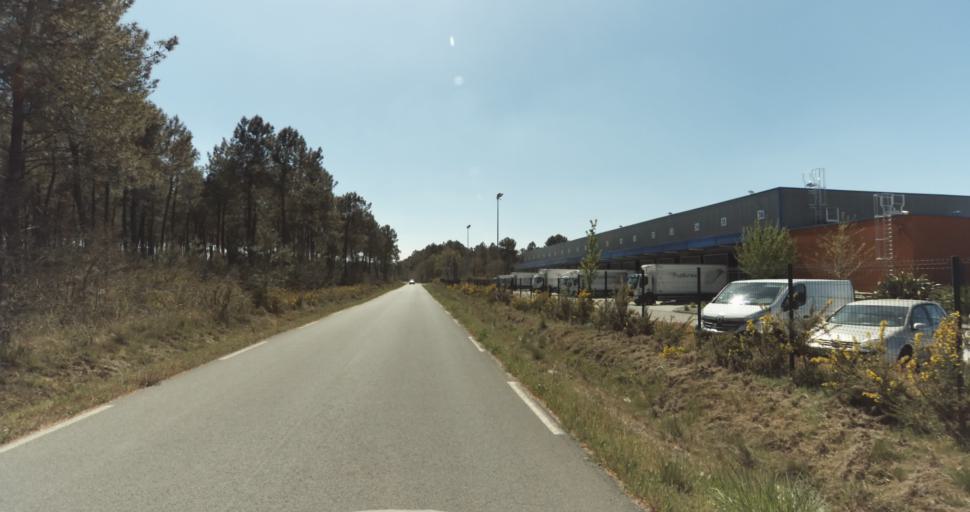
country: FR
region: Aquitaine
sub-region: Departement de la Gironde
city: Martignas-sur-Jalle
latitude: 44.8052
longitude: -0.7525
